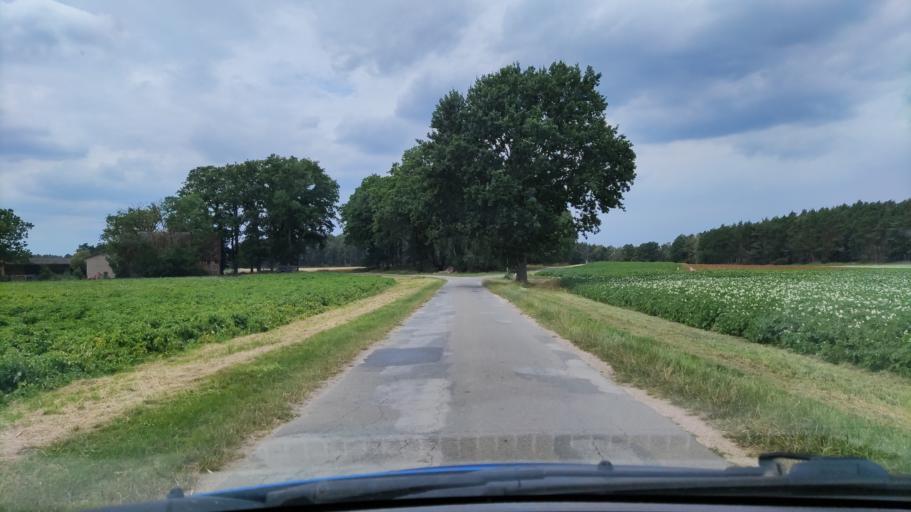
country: DE
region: Lower Saxony
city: Schnega
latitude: 52.9423
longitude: 10.8773
